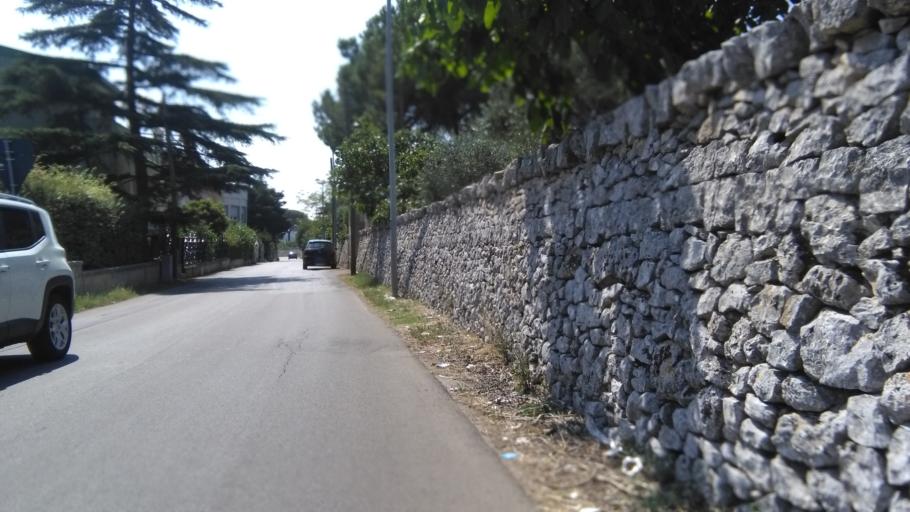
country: IT
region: Apulia
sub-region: Provincia di Bari
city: Putignano
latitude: 40.8457
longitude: 17.1283
